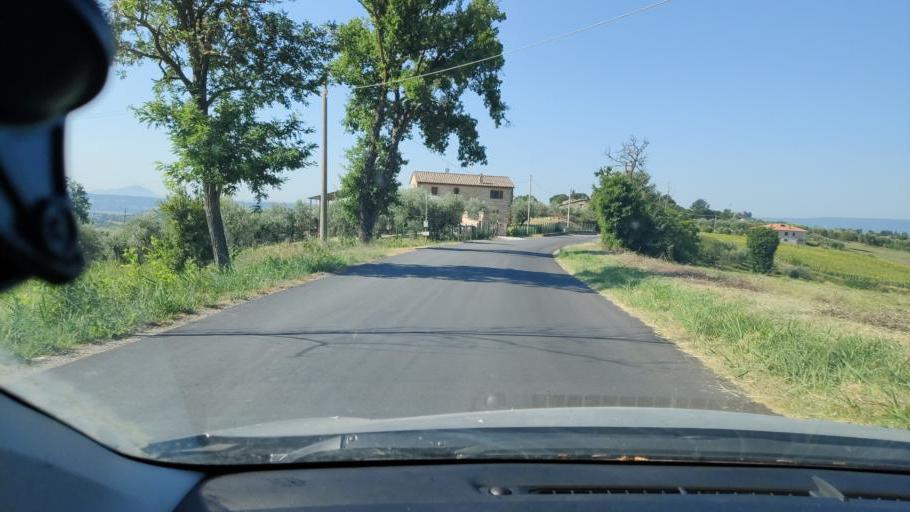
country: IT
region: Umbria
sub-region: Provincia di Terni
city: Fornole
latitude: 42.5339
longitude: 12.4508
